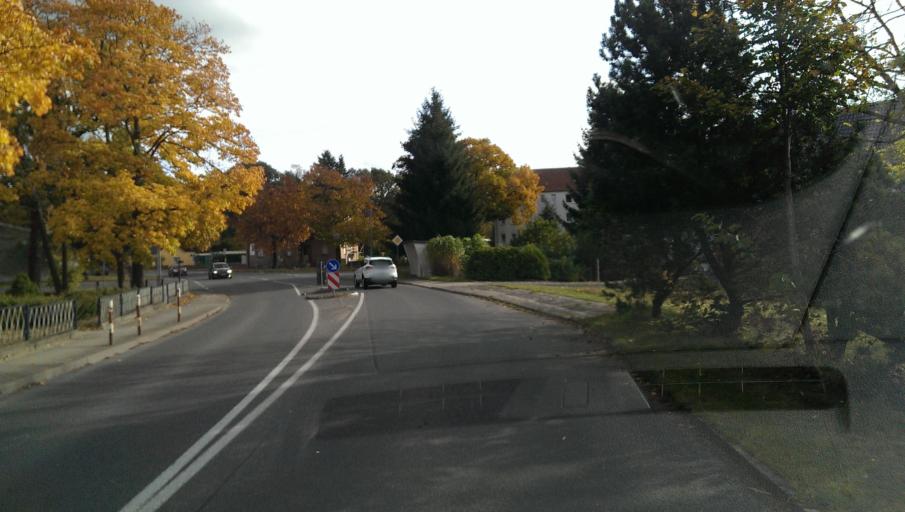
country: DE
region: Saxony
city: Wiednitz
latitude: 51.3874
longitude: 14.0296
